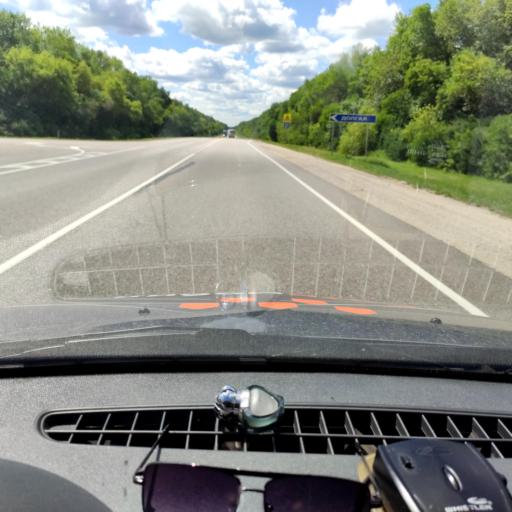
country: RU
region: Lipetsk
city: Borinskoye
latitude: 52.3919
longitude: 39.2296
